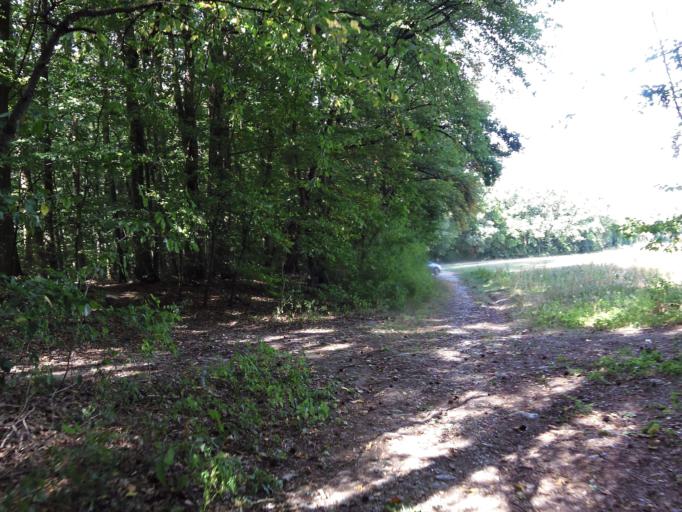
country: DE
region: Bavaria
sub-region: Regierungsbezirk Unterfranken
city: Theilheim
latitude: 49.7487
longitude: 10.0185
